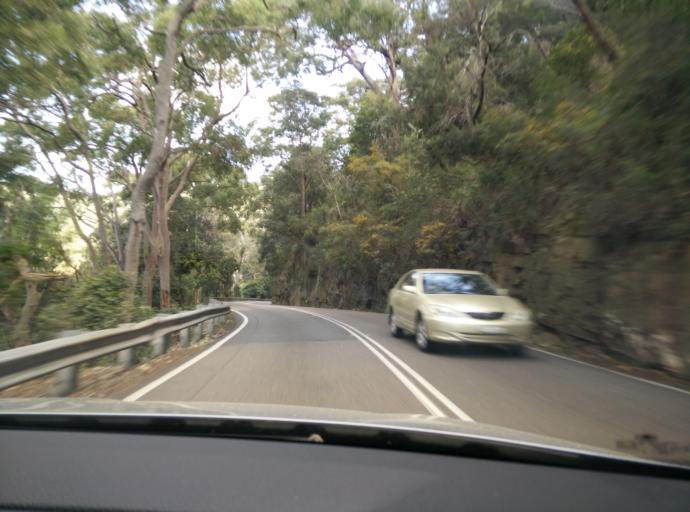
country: AU
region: New South Wales
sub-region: Gosford Shire
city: Blackwall
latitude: -33.4941
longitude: 151.2992
